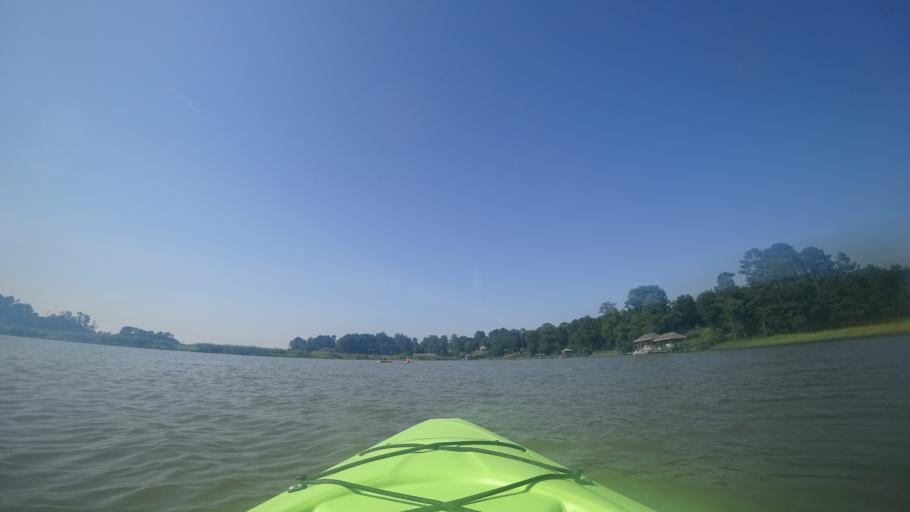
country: US
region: Virginia
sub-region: Isle of Wight County
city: Smithfield
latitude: 36.9719
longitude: -76.6166
